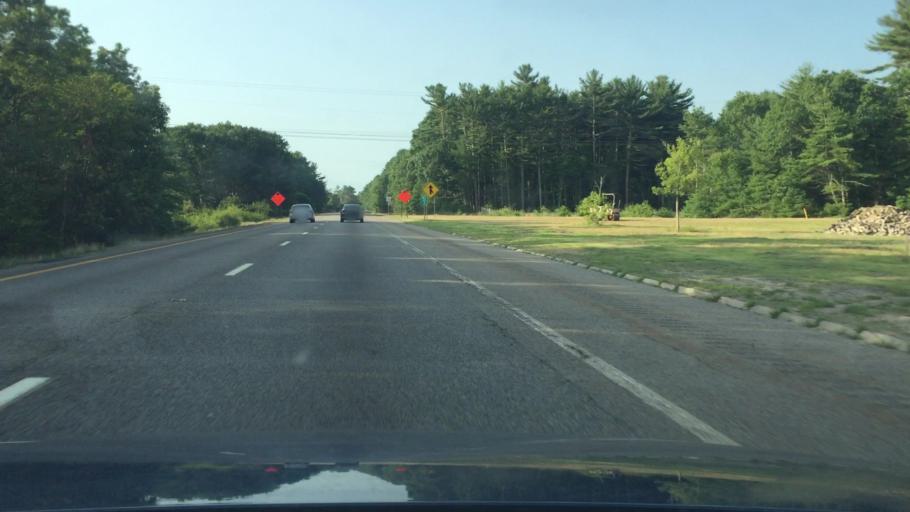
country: US
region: Massachusetts
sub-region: Plymouth County
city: Marshfield
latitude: 42.0543
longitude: -70.7252
